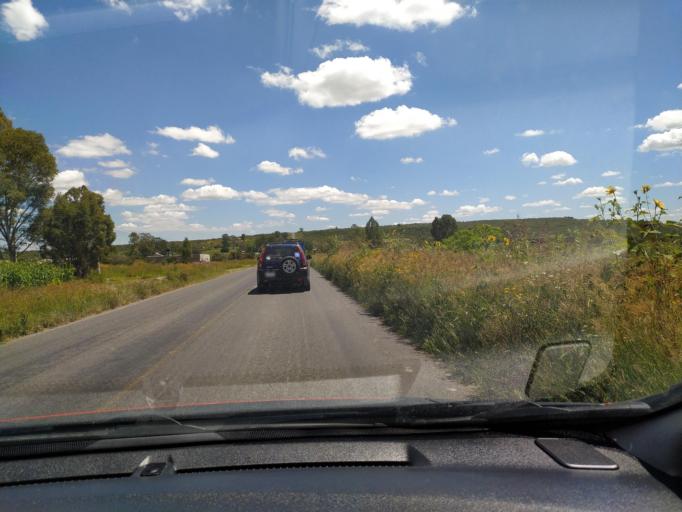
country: MX
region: Jalisco
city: San Diego de Alejandria
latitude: 21.0068
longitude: -102.0369
